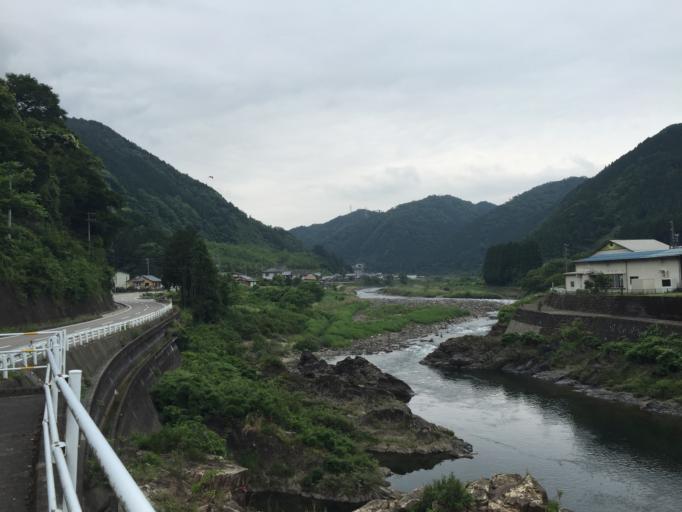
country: JP
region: Gifu
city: Gujo
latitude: 35.7571
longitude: 136.9398
